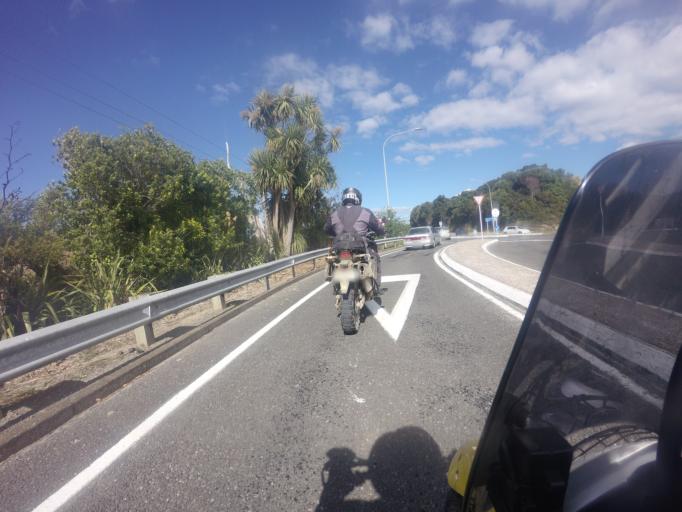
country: NZ
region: Bay of Plenty
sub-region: Whakatane District
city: Whakatane
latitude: -37.9624
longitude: 177.0060
